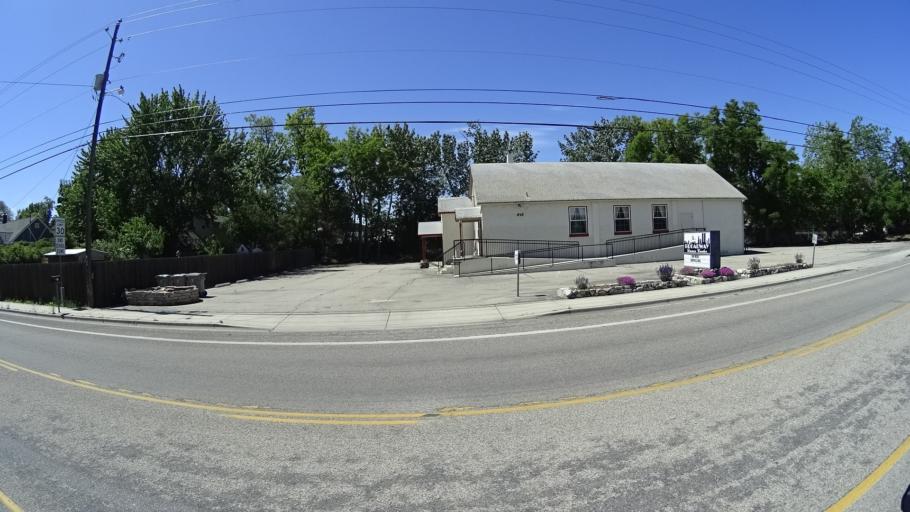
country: US
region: Idaho
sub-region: Ada County
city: Boise
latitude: 43.5780
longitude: -116.1722
